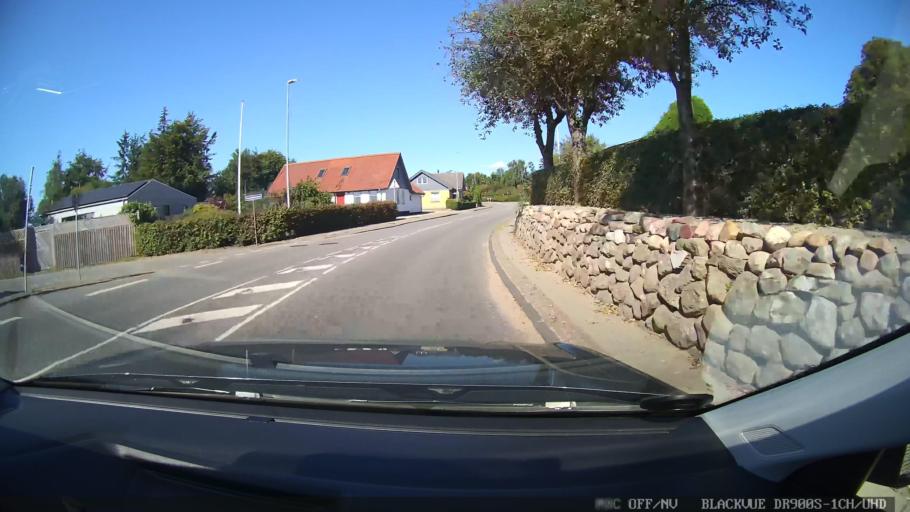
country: DK
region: Central Jutland
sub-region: Randers Kommune
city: Spentrup
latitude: 56.5803
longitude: 9.9950
